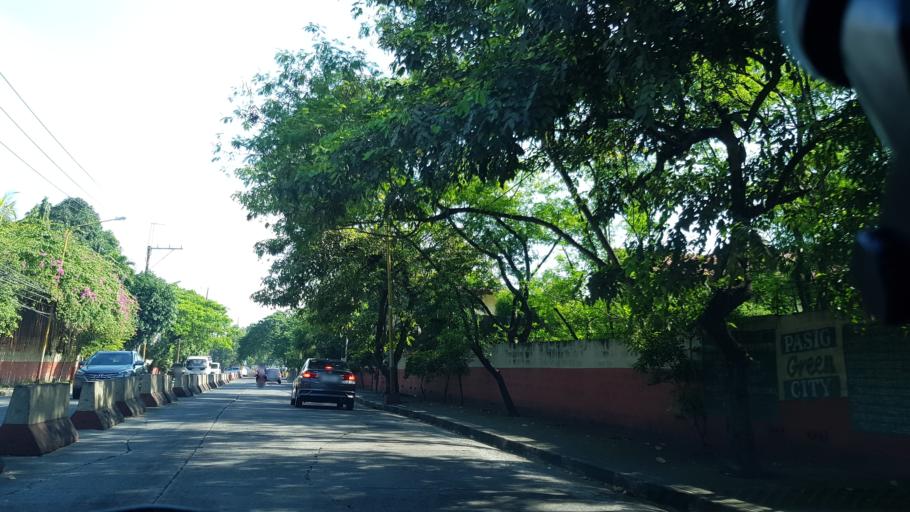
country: PH
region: Metro Manila
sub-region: Pasig
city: Pasig City
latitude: 14.5912
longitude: 121.0724
